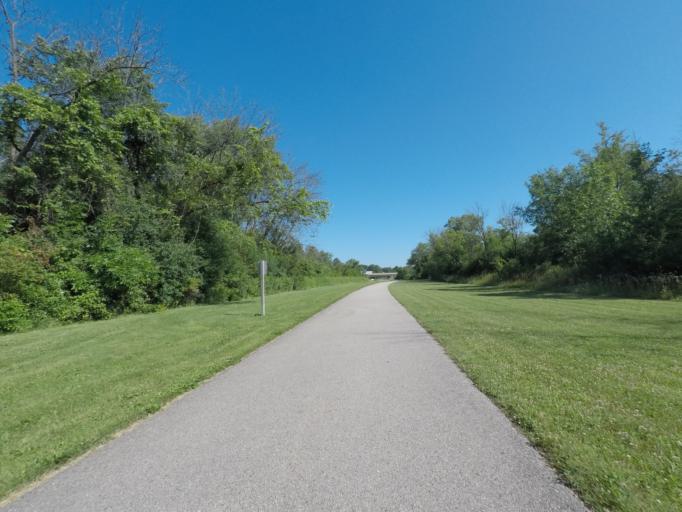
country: US
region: Wisconsin
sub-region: Waukesha County
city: Elm Grove
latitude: 43.0267
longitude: -88.0659
